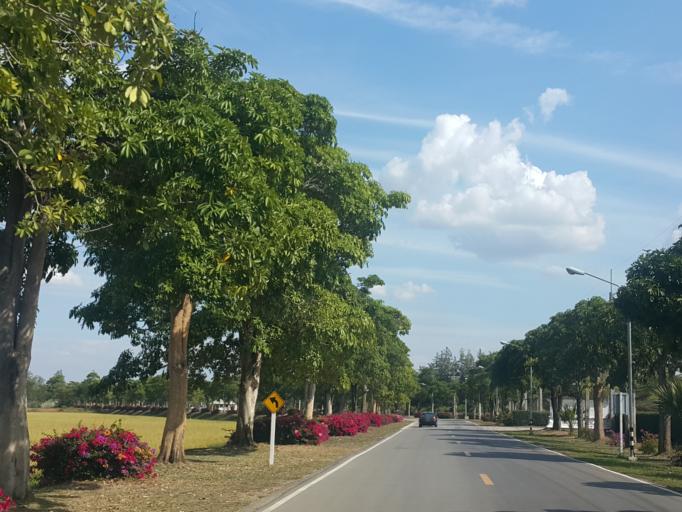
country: TH
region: Sukhothai
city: Si Samrong
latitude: 17.2277
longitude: 99.8297
